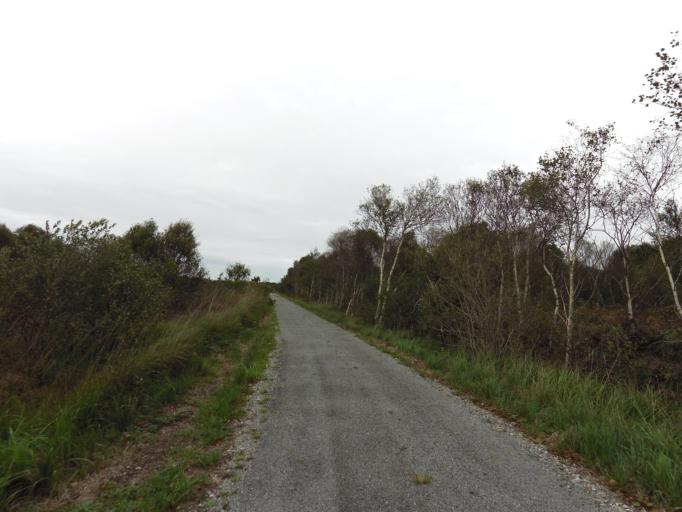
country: IE
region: Leinster
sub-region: Uibh Fhaili
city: Ferbane
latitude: 53.2401
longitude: -7.7574
